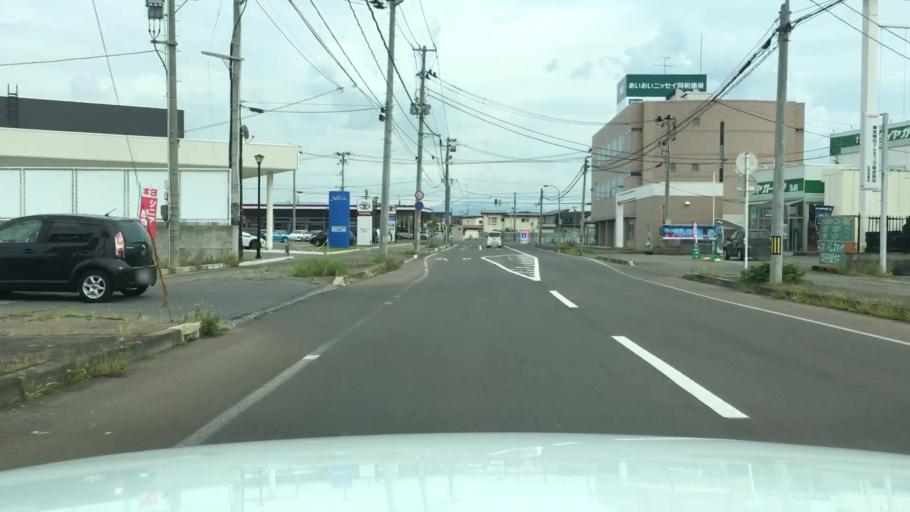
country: JP
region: Aomori
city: Hirosaki
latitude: 40.6152
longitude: 140.4893
